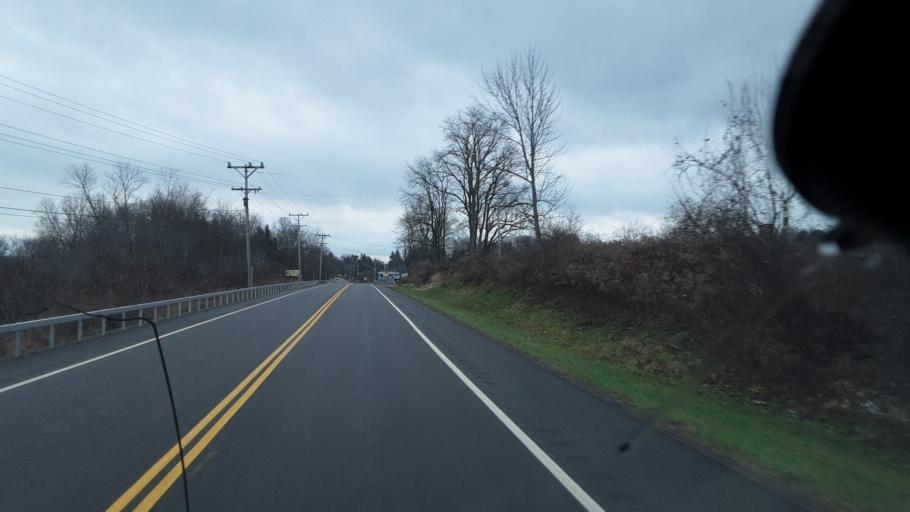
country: US
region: New York
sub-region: Allegany County
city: Houghton
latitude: 42.3505
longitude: -78.1219
